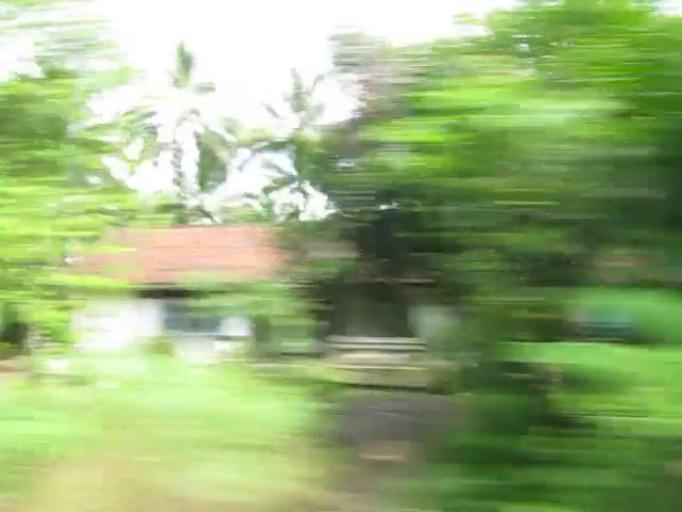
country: ID
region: Central Java
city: Meluwung
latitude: -7.3928
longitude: 108.6985
